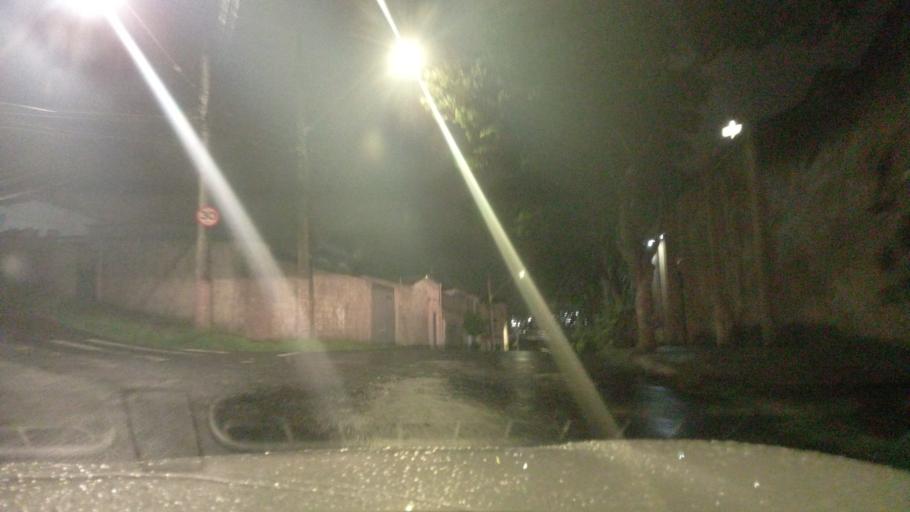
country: BR
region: Minas Gerais
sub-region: Belo Horizonte
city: Belo Horizonte
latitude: -19.8828
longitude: -43.9181
